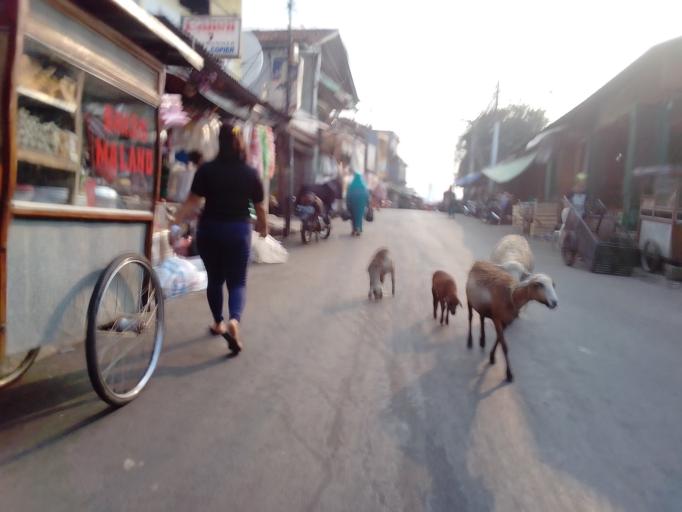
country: ID
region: Jakarta Raya
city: Jakarta
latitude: -6.1934
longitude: 106.8137
